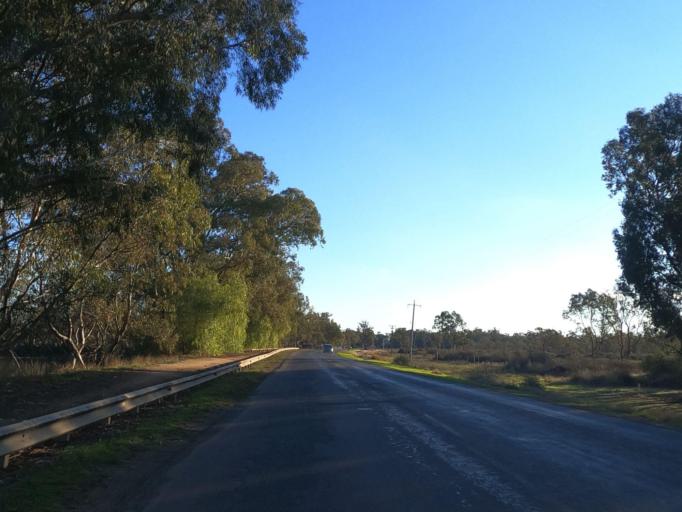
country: AU
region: Victoria
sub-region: Swan Hill
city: Swan Hill
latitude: -35.3364
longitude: 143.5734
